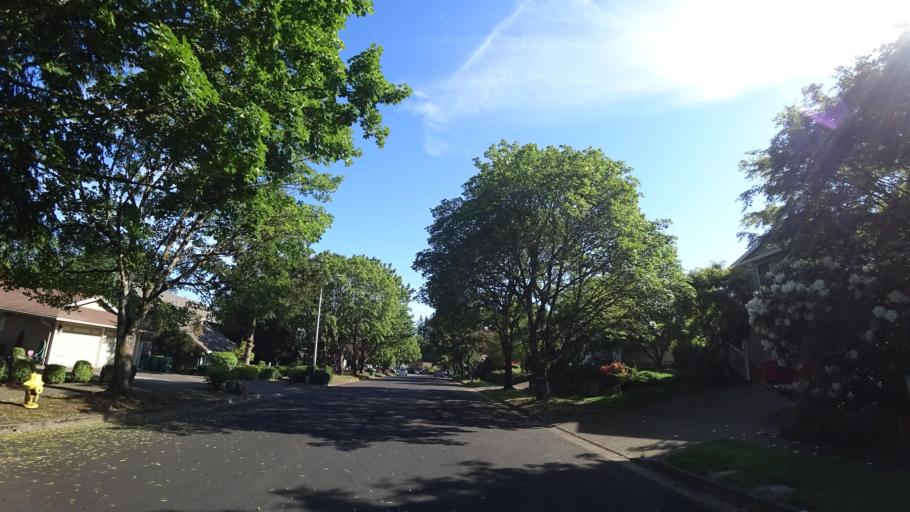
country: US
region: Oregon
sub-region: Washington County
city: Beaverton
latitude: 45.4565
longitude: -122.8062
